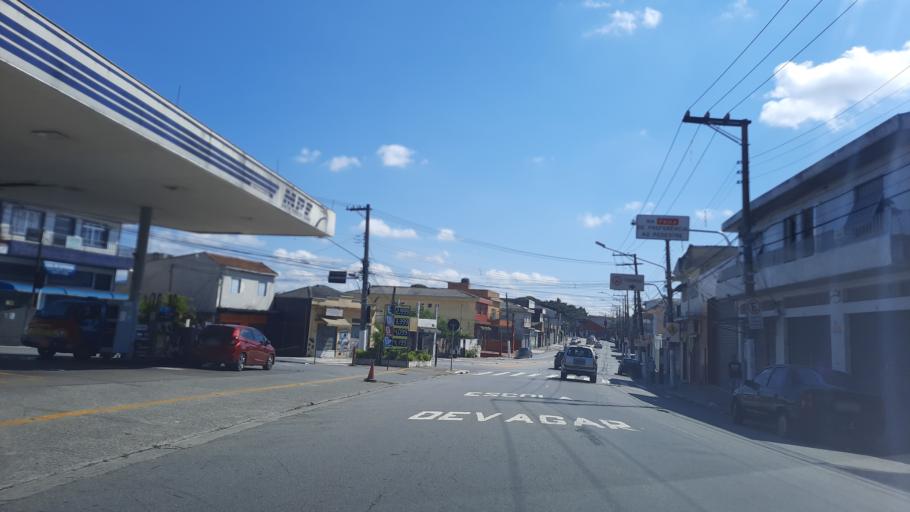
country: BR
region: Sao Paulo
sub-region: Sao Paulo
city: Sao Paulo
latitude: -23.4926
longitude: -46.6776
